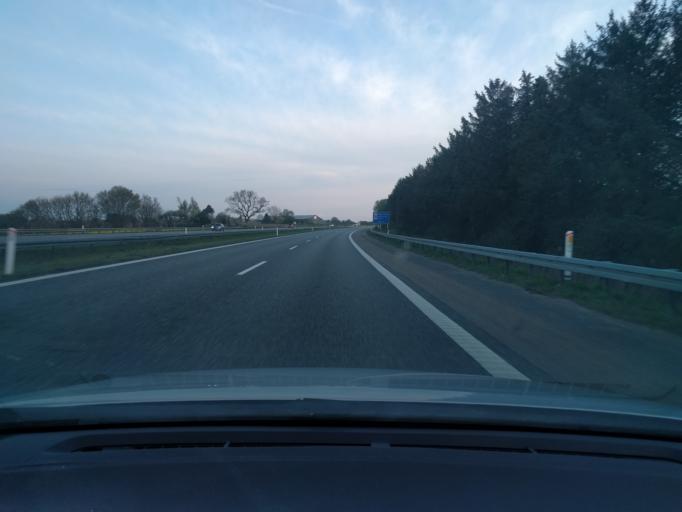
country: DK
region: Zealand
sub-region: Faxe Kommune
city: Ronnede
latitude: 55.2699
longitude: 12.0069
